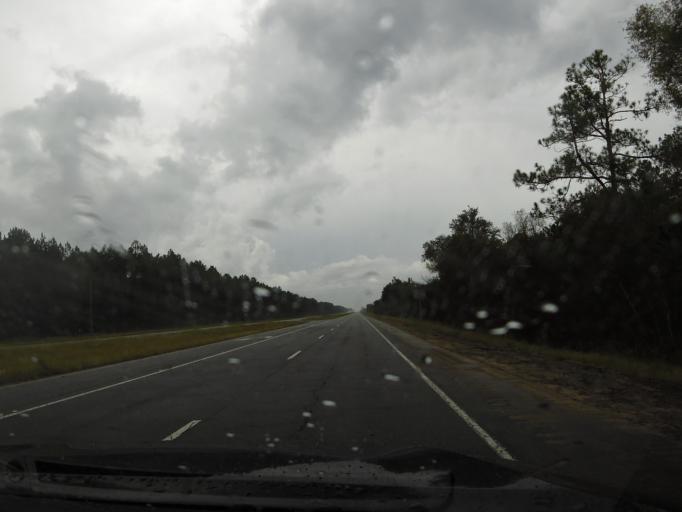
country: US
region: Georgia
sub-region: Wayne County
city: Jesup
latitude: 31.4488
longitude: -81.6957
